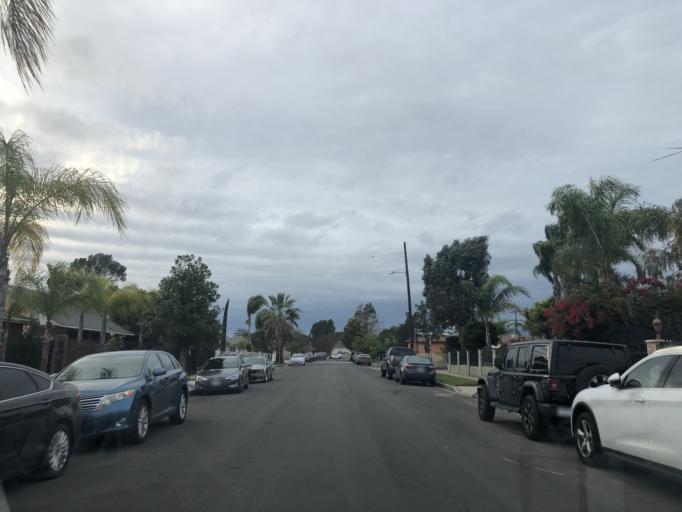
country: US
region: California
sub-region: Los Angeles County
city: North Hollywood
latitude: 34.2107
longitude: -118.3501
